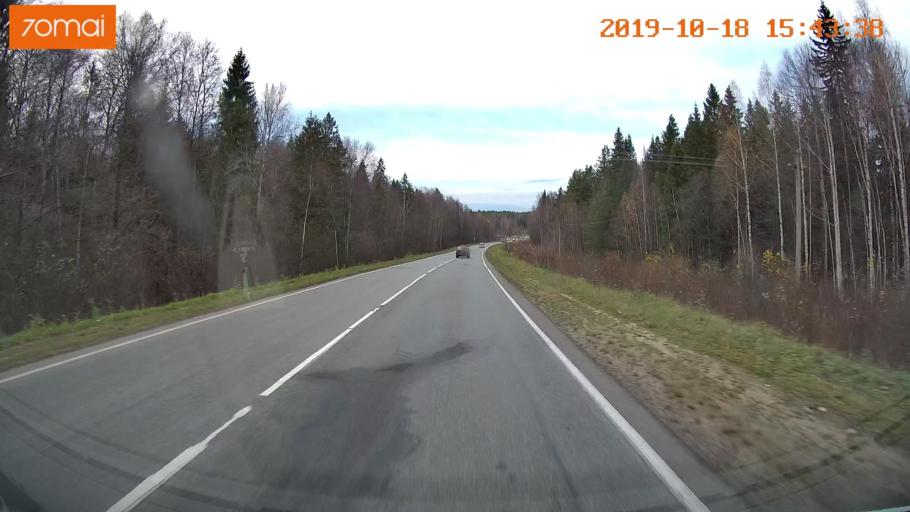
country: RU
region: Vladimir
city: Golovino
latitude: 55.9705
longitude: 40.5488
